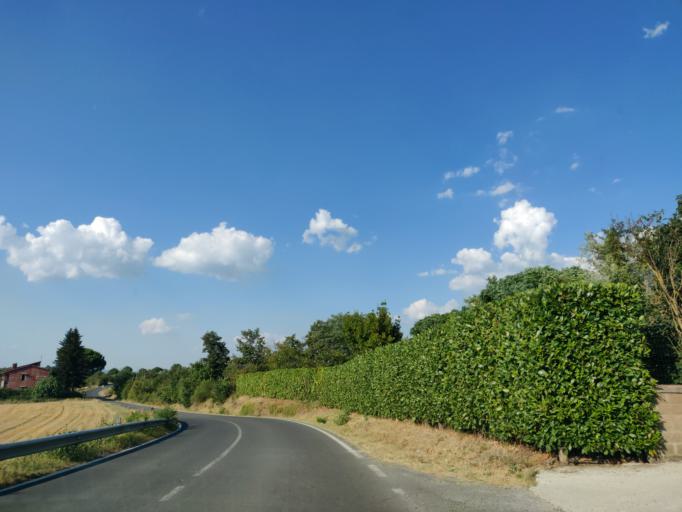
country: IT
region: Latium
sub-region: Provincia di Viterbo
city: Gradoli
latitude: 42.6606
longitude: 11.8519
